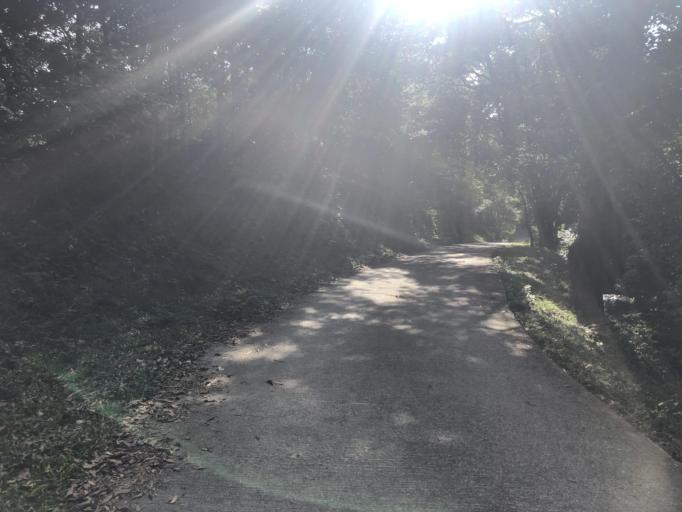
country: HK
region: Tsuen Wan
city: Tsuen Wan
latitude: 22.4010
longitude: 114.0951
